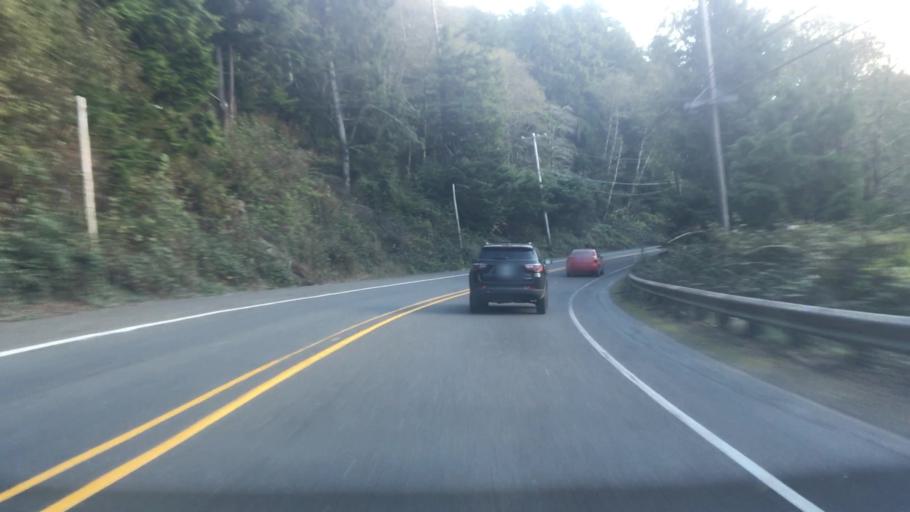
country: US
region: Oregon
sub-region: Clatsop County
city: Seaside
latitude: 45.9566
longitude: -123.9263
